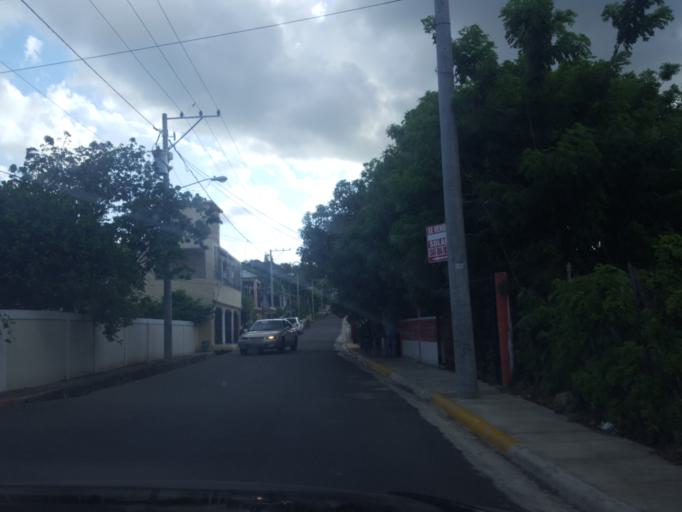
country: DO
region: Santiago
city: Licey al Medio
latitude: 19.3739
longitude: -70.6387
